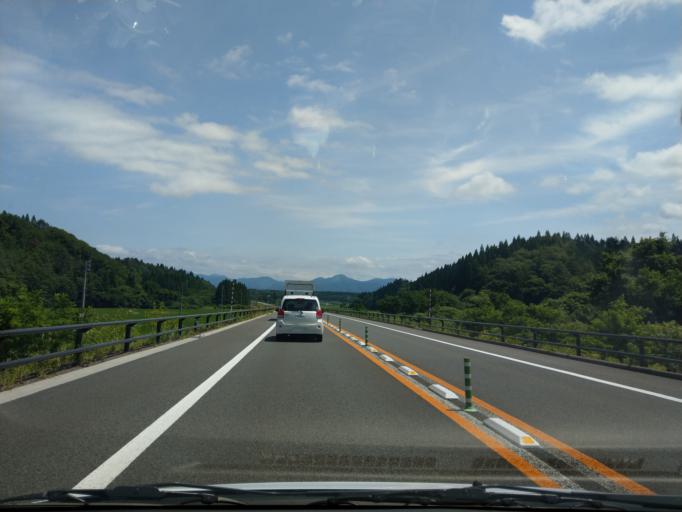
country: JP
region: Akita
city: Odate
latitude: 40.2311
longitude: 140.4903
